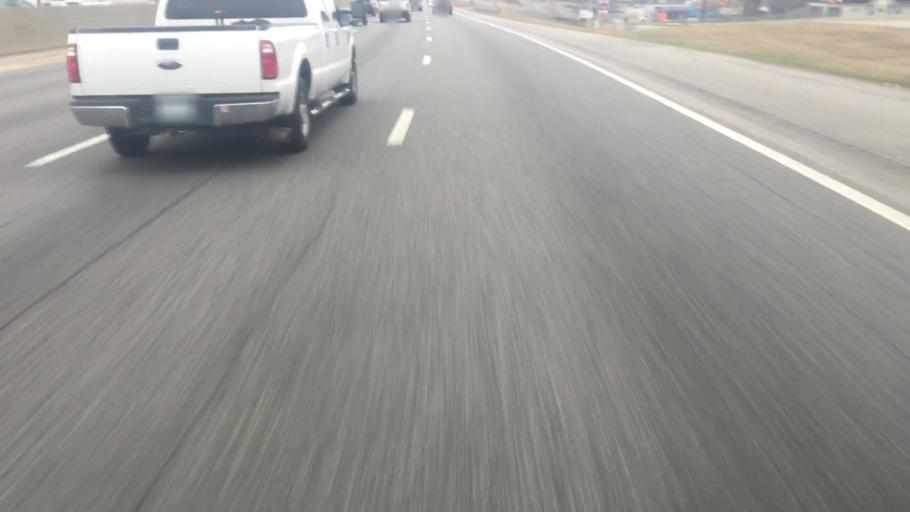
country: US
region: Alabama
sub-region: Jefferson County
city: Birmingham
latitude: 33.5538
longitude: -86.8311
